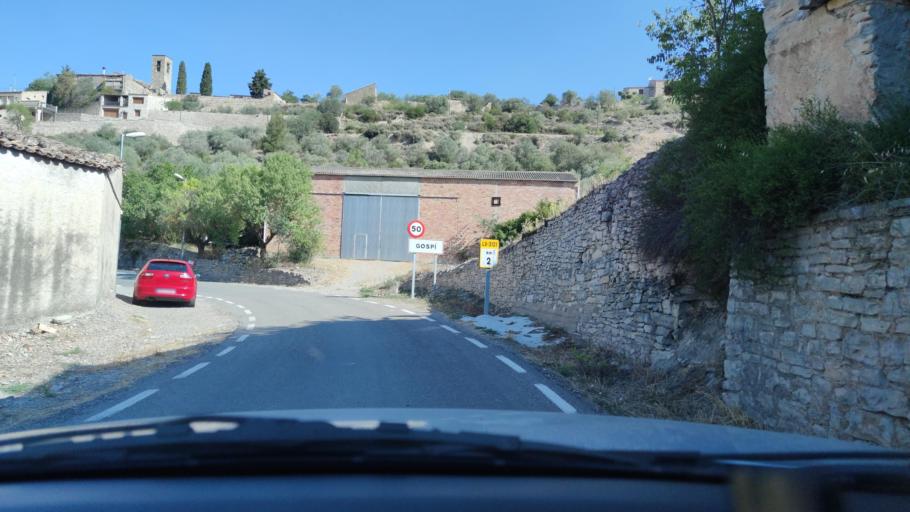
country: ES
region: Catalonia
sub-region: Provincia de Lleida
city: Ivorra
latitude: 41.7376
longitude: 1.3520
